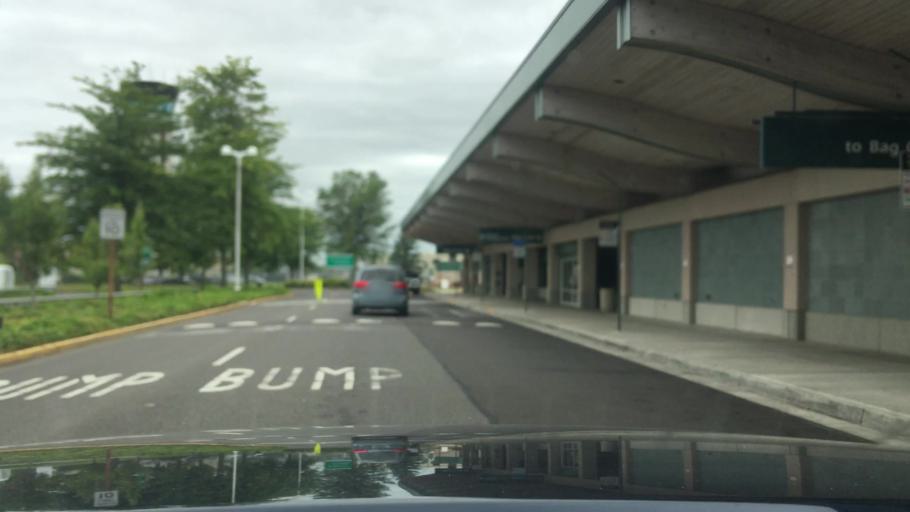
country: US
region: Oregon
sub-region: Lane County
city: Junction City
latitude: 44.1190
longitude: -123.2121
